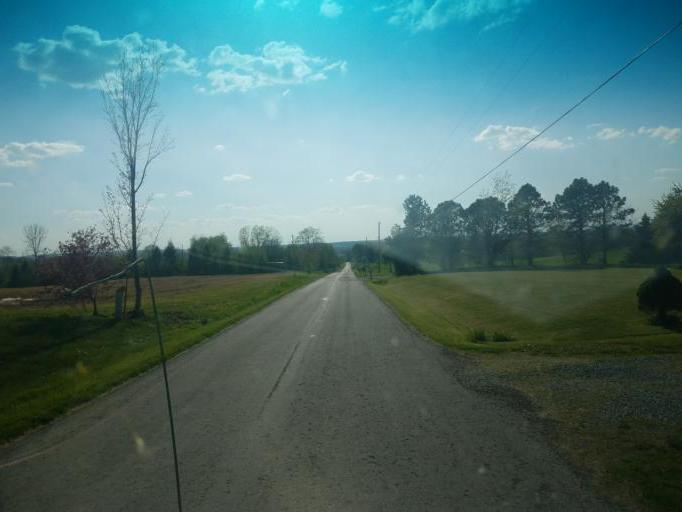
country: US
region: Ohio
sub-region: Wayne County
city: Wooster
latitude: 40.7481
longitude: -81.9167
